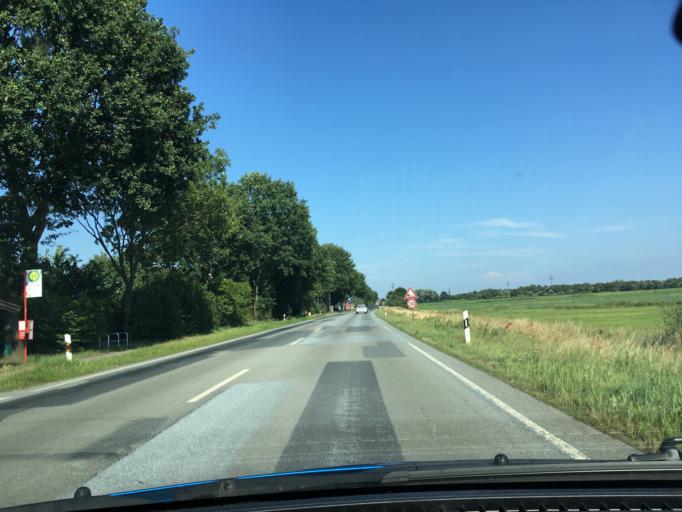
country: DE
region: Lower Saxony
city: Winsen
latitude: 53.3669
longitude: 10.1695
